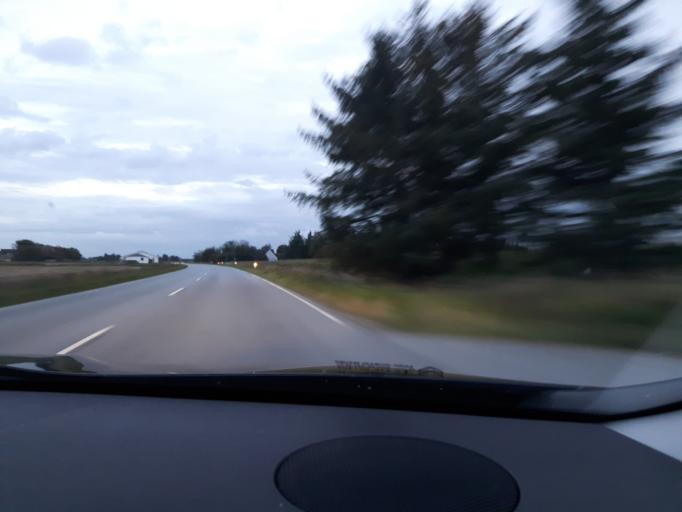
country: DK
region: North Denmark
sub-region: Hjorring Kommune
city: Hjorring
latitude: 57.5042
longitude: 9.9433
